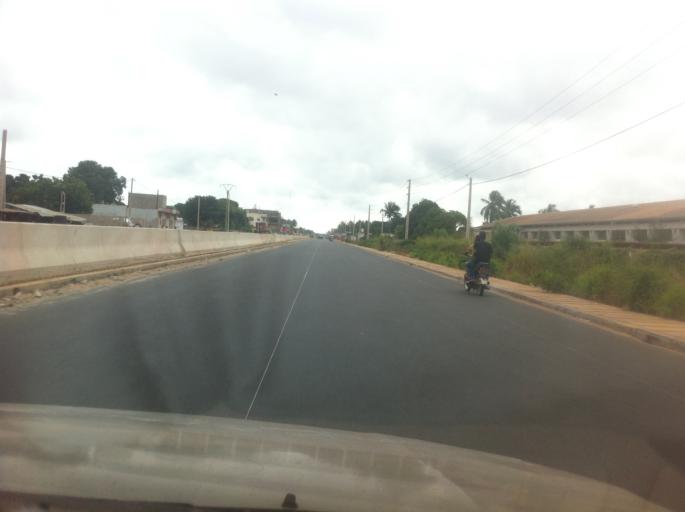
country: BJ
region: Atlantique
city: Ouidah
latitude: 6.3732
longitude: 2.0778
